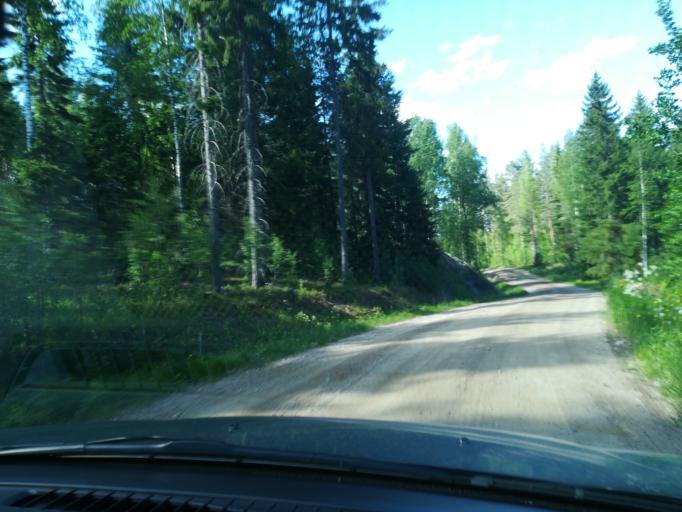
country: FI
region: Southern Savonia
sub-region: Mikkeli
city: Puumala
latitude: 61.6502
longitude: 28.1777
